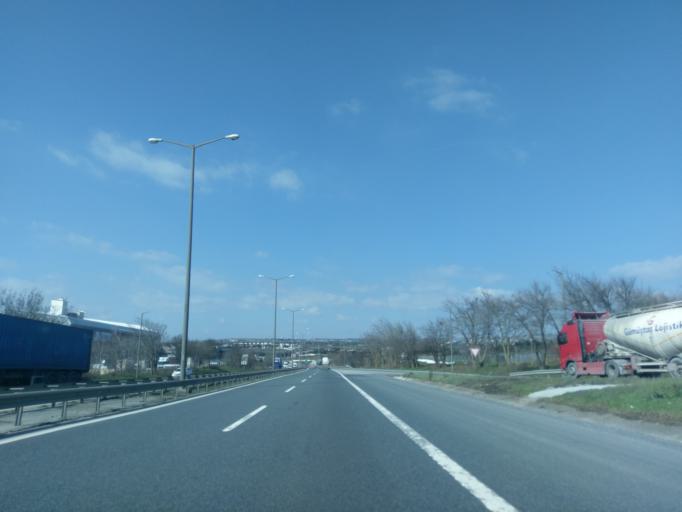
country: TR
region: Istanbul
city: Ortakoy
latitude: 41.0865
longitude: 28.3672
